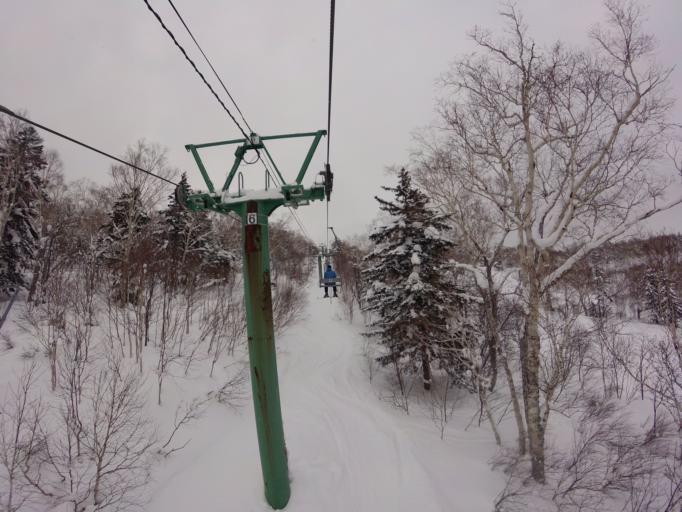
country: JP
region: Hokkaido
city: Sapporo
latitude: 43.0711
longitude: 141.2045
